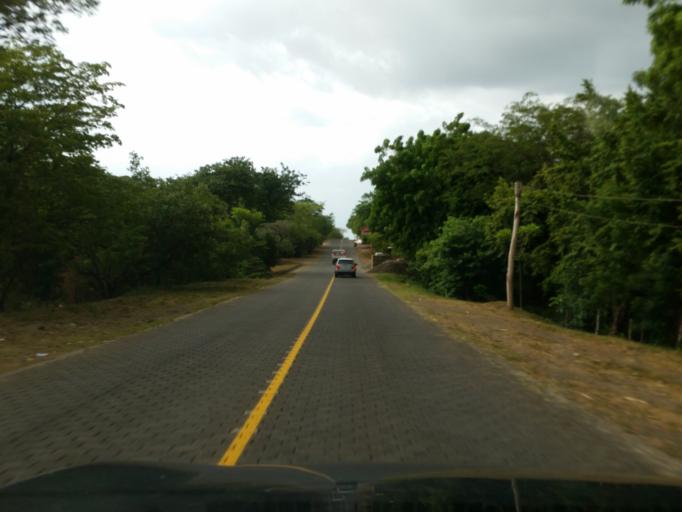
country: NI
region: Managua
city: Carlos Fonseca Amador
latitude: 11.9761
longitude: -86.5145
